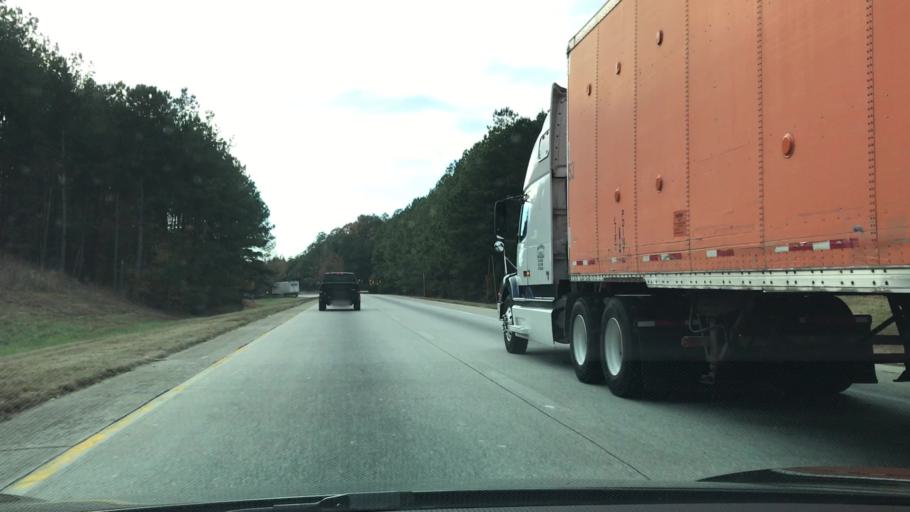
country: US
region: Georgia
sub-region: DeKalb County
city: Gresham Park
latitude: 33.6759
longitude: -84.3250
